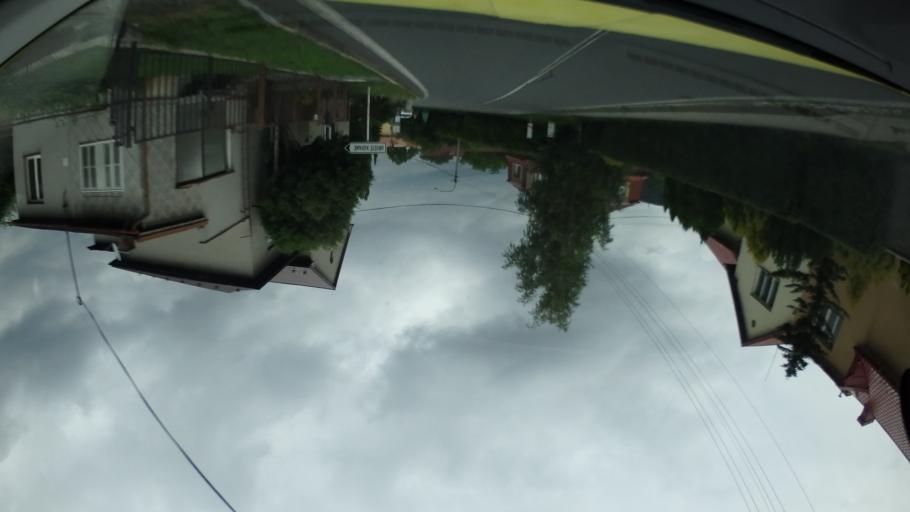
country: CZ
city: Stramberk
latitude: 49.5814
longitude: 18.1273
